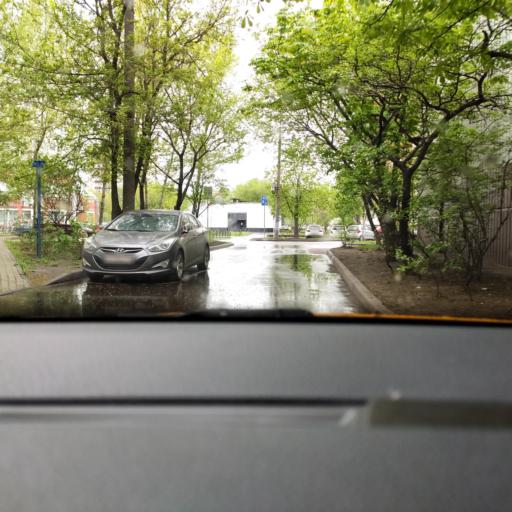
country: RU
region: Moscow
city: Vykhino-Zhulebino
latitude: 55.6956
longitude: 37.8137
